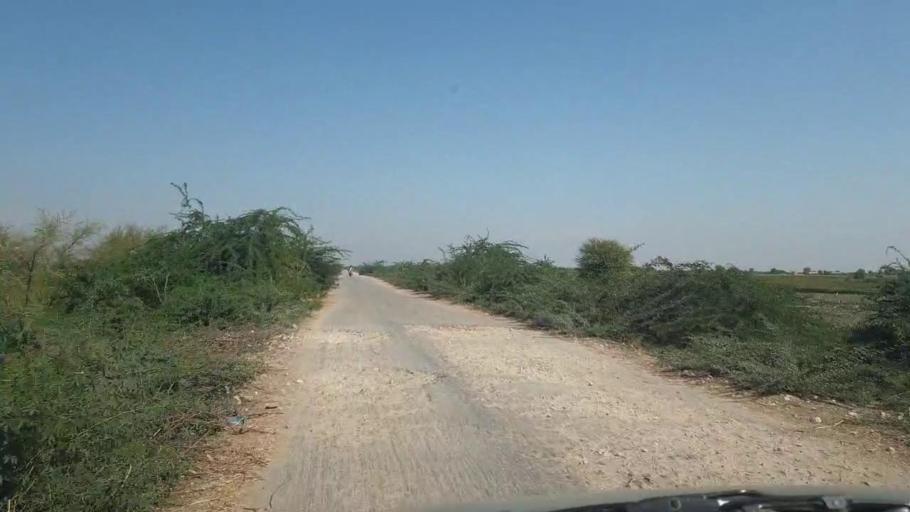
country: PK
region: Sindh
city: Tando Bago
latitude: 24.8276
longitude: 68.9881
